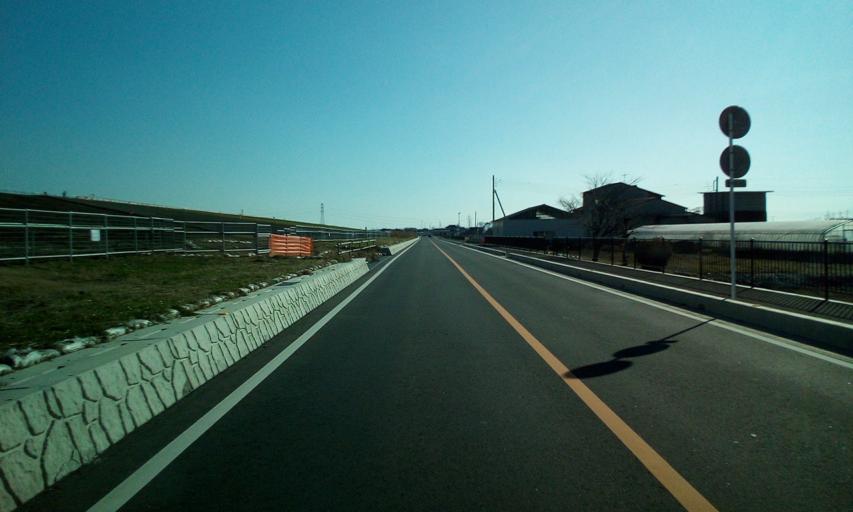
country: JP
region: Ibaraki
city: Sakai
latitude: 36.0750
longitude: 139.7786
